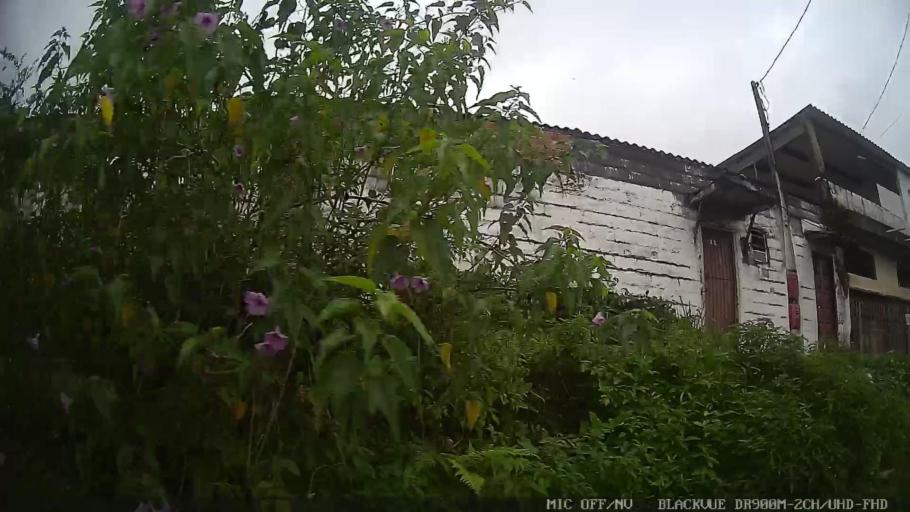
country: BR
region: Sao Paulo
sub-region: Itanhaem
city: Itanhaem
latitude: -24.1800
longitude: -46.8194
